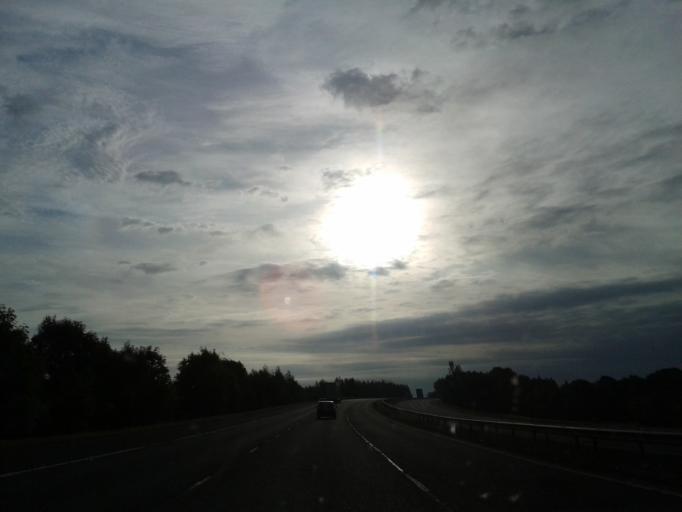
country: GB
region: Scotland
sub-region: Dumfries and Galloway
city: Gretna
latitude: 55.0072
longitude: -3.0727
